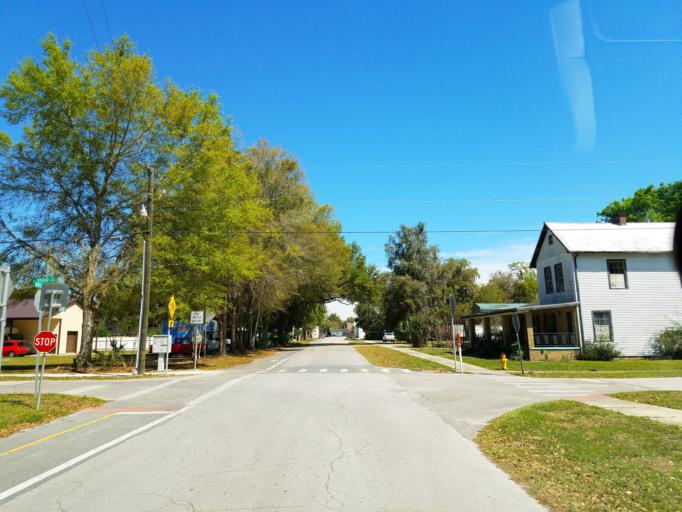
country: US
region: Florida
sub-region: Sumter County
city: Bushnell
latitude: 28.6642
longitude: -82.1151
